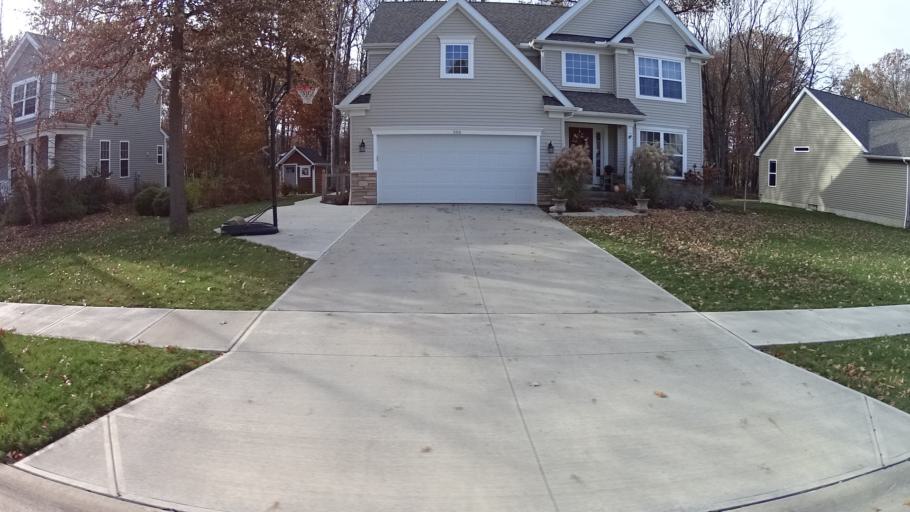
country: US
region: Ohio
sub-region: Lorain County
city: Avon Lake
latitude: 41.5029
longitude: -81.9767
